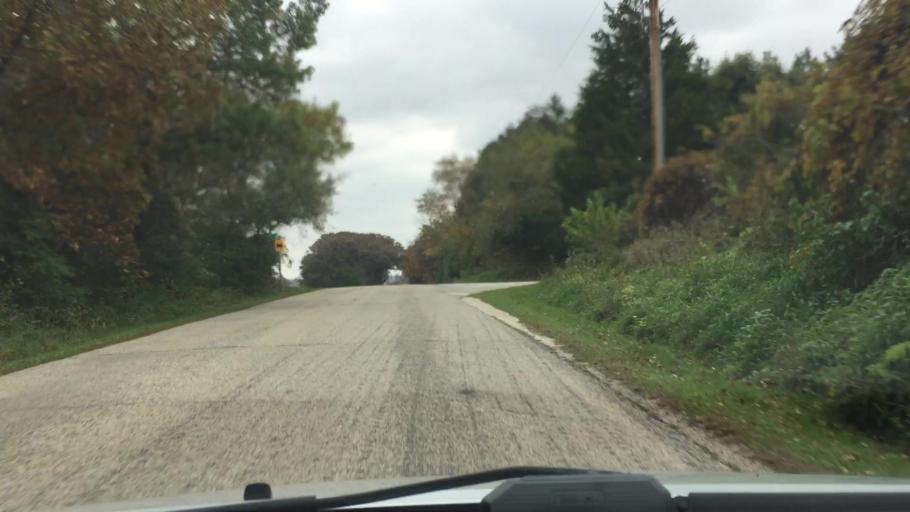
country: US
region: Wisconsin
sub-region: Walworth County
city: Whitewater
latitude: 42.8353
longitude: -88.7968
